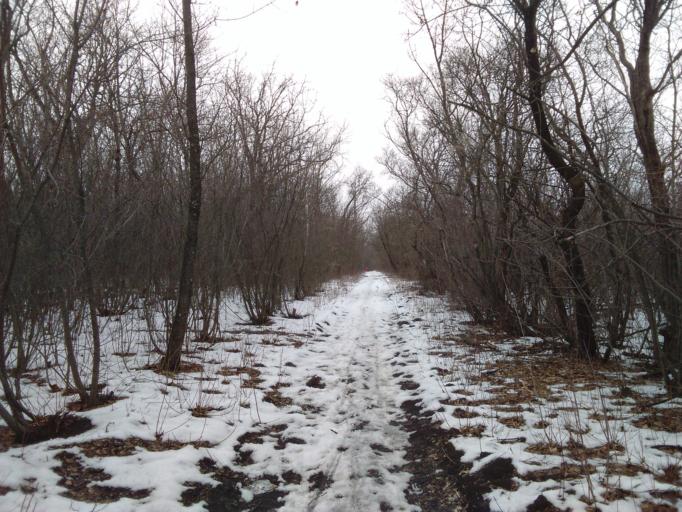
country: RU
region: Rostov
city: Temernik
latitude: 47.3535
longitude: 39.7398
